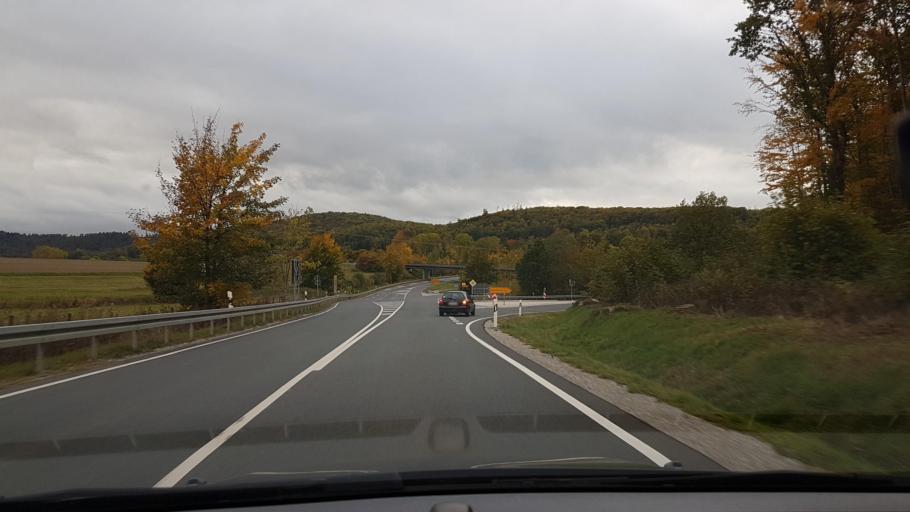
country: DE
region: Lower Saxony
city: Gittelde
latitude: 51.8302
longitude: 10.1988
